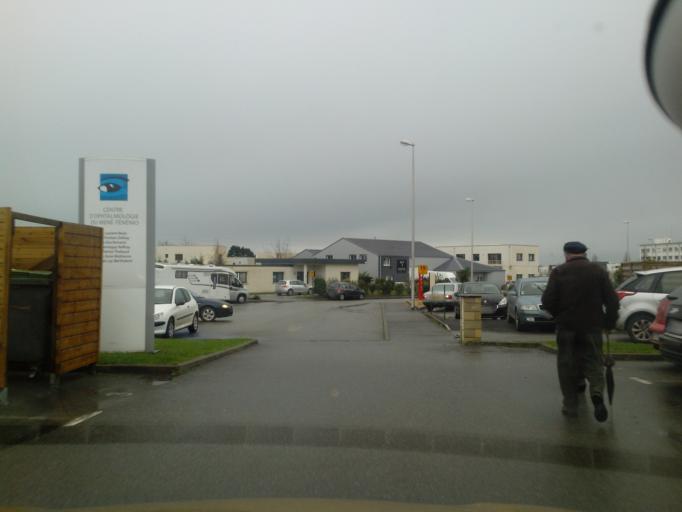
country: FR
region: Brittany
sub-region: Departement du Morbihan
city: Vannes
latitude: 47.6817
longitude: -2.7738
